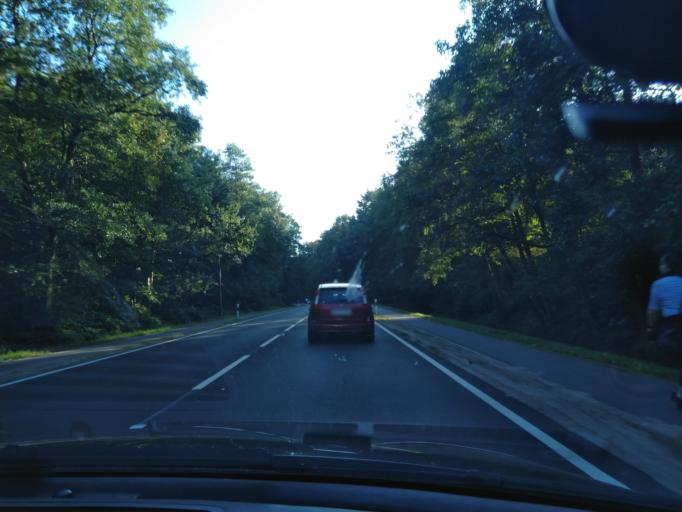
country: DE
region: Lower Saxony
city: Leer
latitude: 53.2548
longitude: 7.4575
